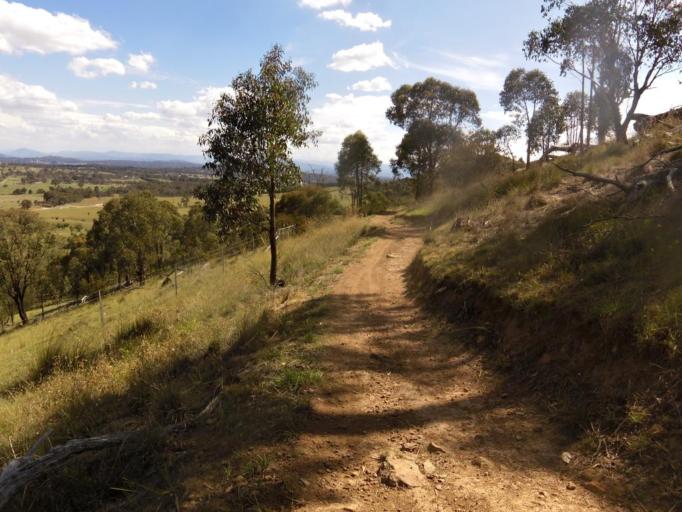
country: AU
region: Australian Capital Territory
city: Belconnen
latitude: -35.1568
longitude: 149.0810
